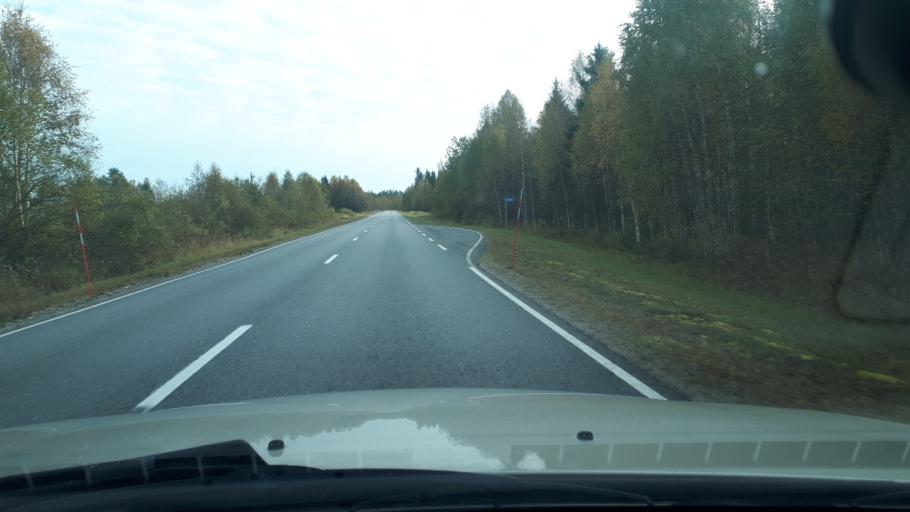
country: FI
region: Lapland
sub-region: Rovaniemi
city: Ranua
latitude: 65.9612
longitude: 26.0522
